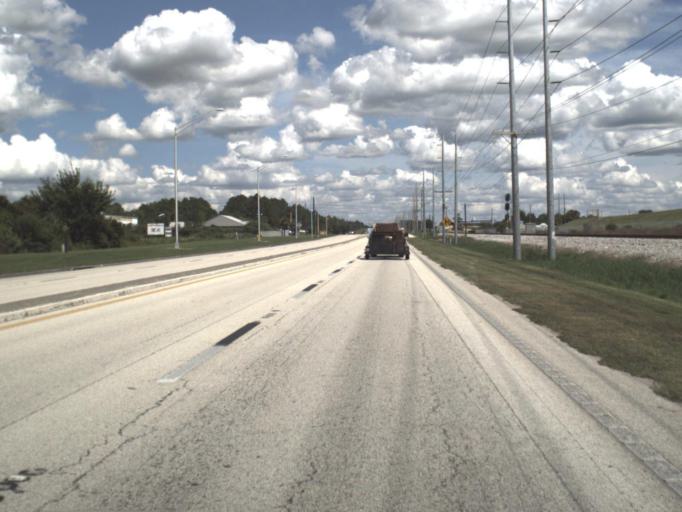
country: US
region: Florida
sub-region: Polk County
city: Mulberry
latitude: 27.8944
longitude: -81.9464
